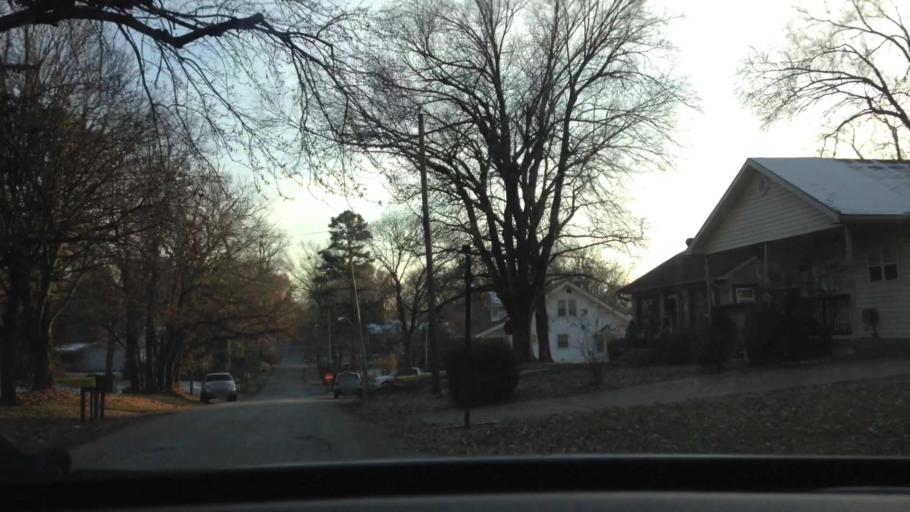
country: US
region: Missouri
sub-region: Clay County
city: North Kansas City
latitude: 39.1624
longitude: -94.5393
